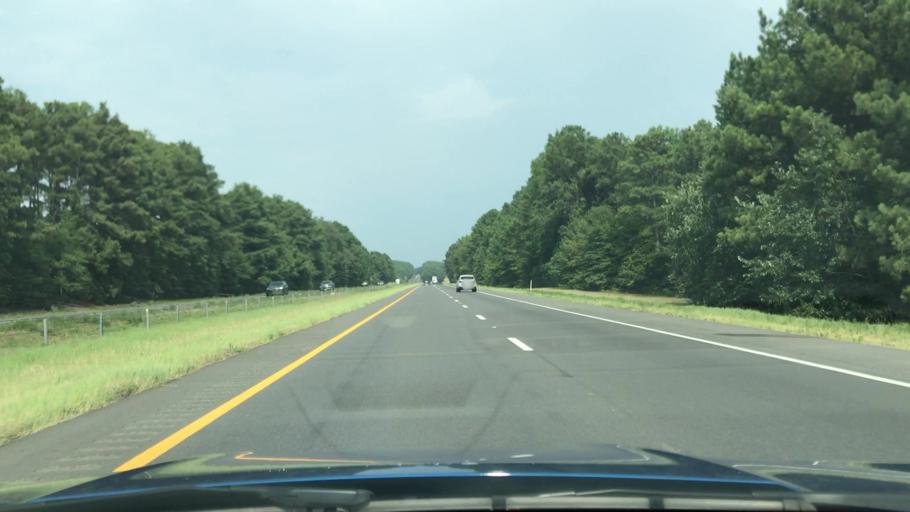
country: US
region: Texas
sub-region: Harrison County
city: Hallsville
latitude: 32.4676
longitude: -94.6149
